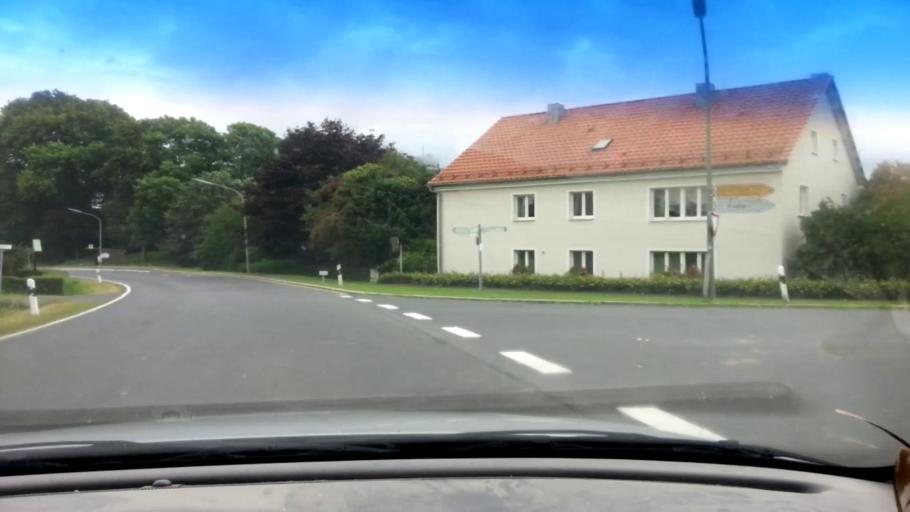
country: DE
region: Bavaria
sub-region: Upper Palatinate
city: Waldsassen
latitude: 50.0360
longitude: 12.2910
